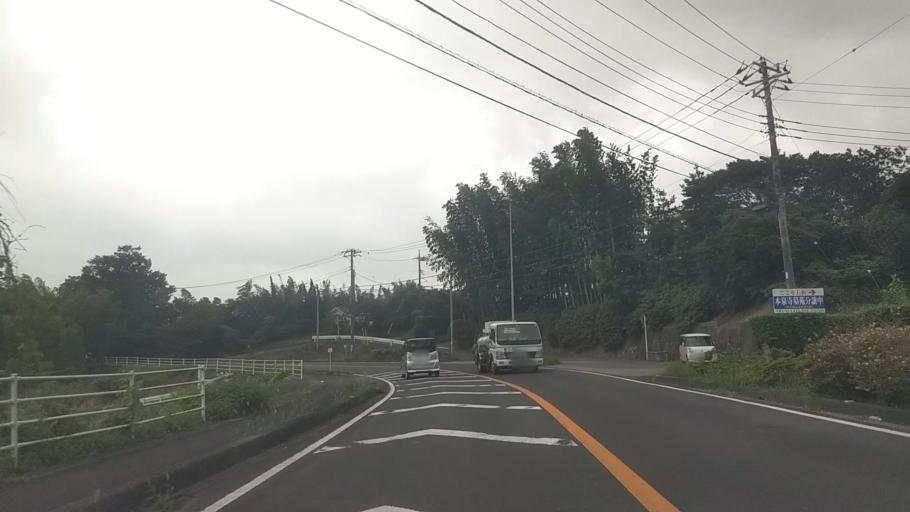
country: JP
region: Chiba
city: Ohara
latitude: 35.2824
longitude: 140.3206
